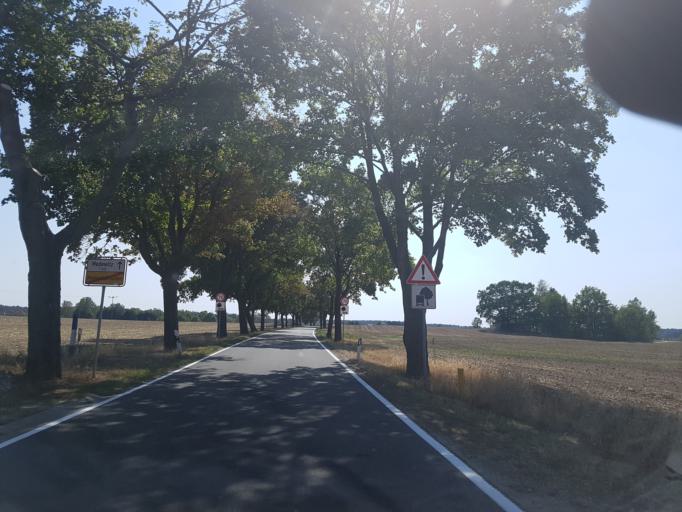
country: DE
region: Brandenburg
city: Wiesenburg
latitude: 52.0656
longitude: 12.3846
